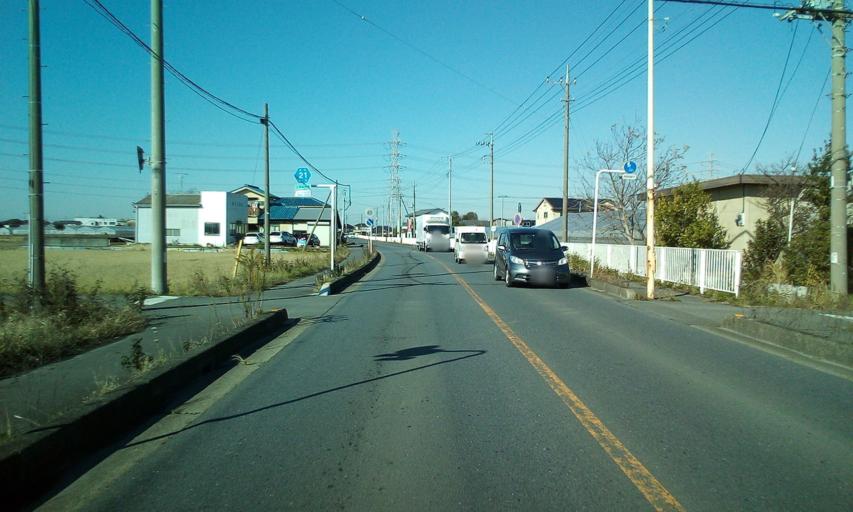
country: JP
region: Saitama
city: Yoshikawa
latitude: 35.8971
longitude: 139.8732
